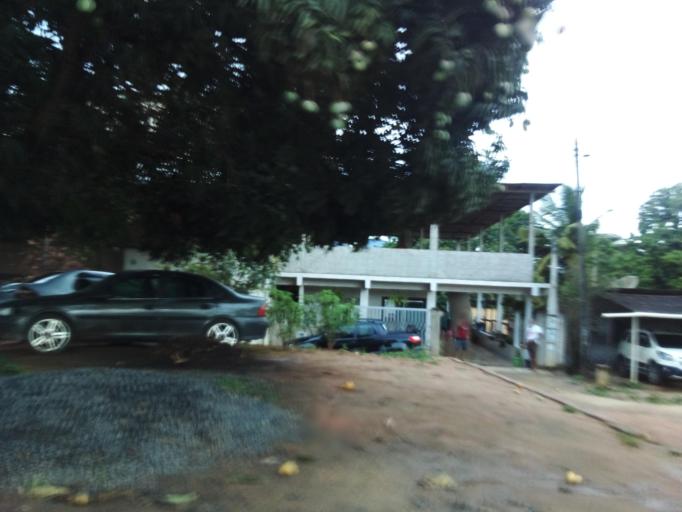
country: BR
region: Espirito Santo
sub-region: Marilandia
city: Marilandia
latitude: -19.5350
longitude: -40.4868
